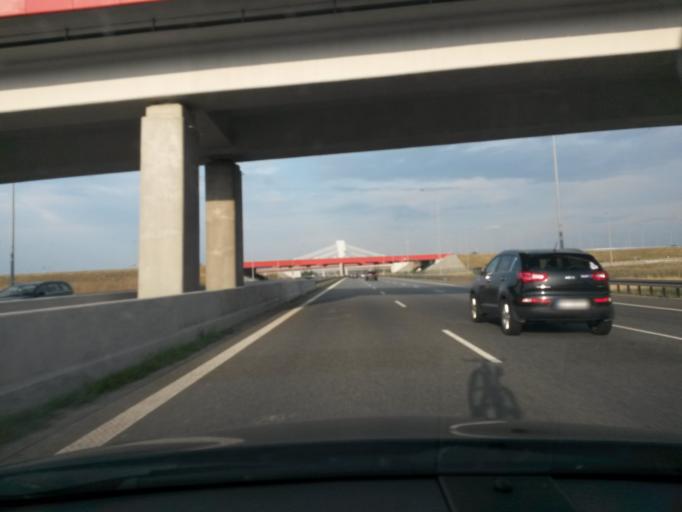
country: PL
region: Lodz Voivodeship
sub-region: Powiat zgierski
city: Strykow
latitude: 51.8913
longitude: 19.6309
